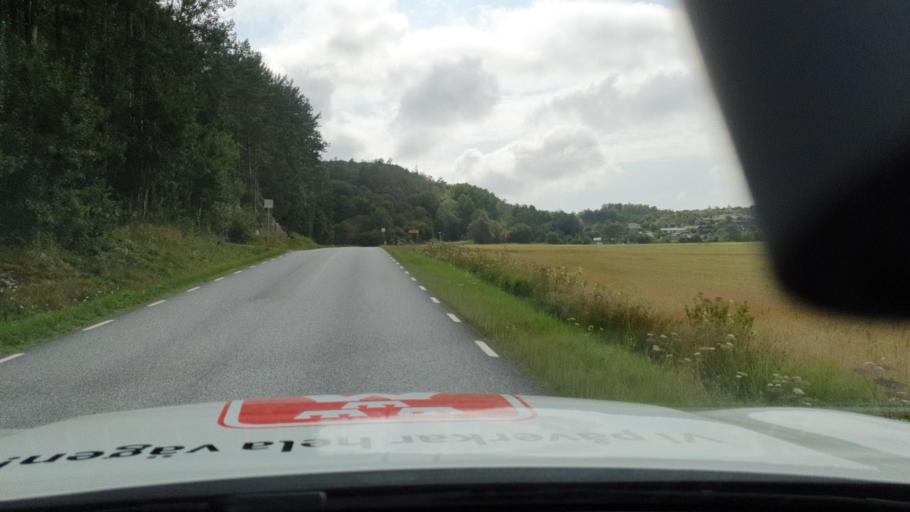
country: SE
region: Vaestra Goetaland
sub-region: Sotenas Kommun
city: Hunnebostrand
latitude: 58.5701
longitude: 11.3109
